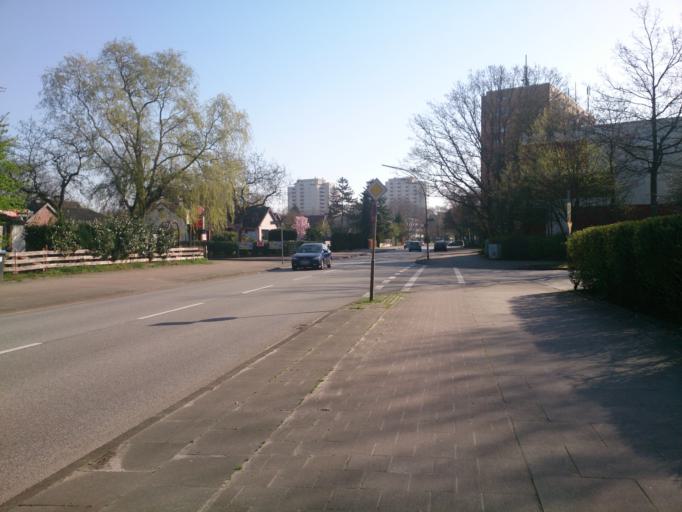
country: DE
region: Lower Saxony
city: Neu Wulmstorf
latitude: 53.4763
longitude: 9.8696
